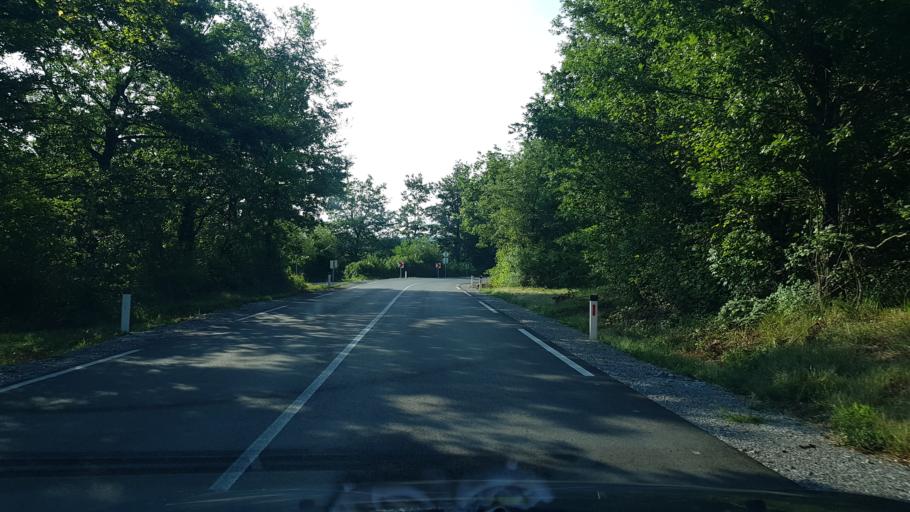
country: SI
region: Divaca
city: Divaca
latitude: 45.6710
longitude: 14.0174
